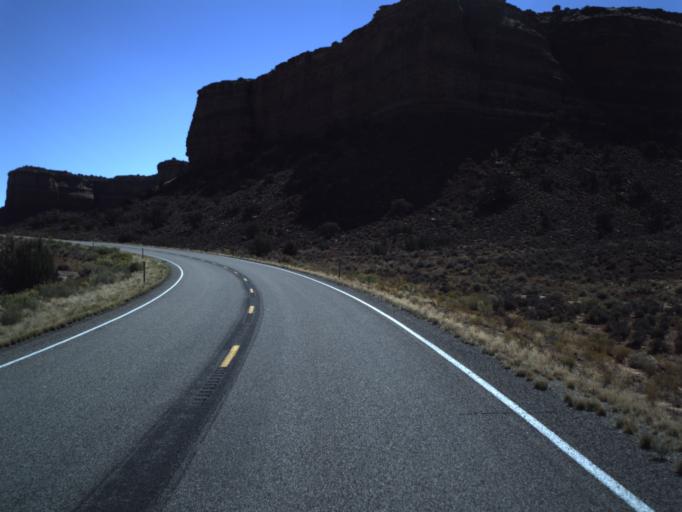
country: US
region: Utah
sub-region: San Juan County
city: Blanding
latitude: 37.7372
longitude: -110.2727
